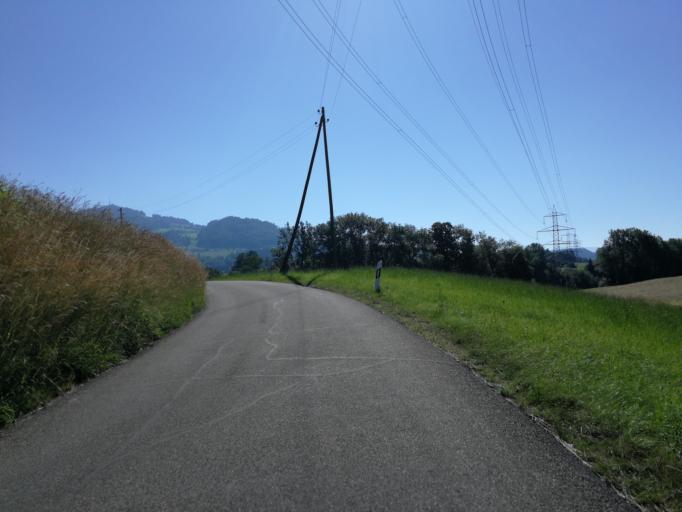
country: CH
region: Zurich
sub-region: Bezirk Hinwil
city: Durnten
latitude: 47.2846
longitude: 8.8383
